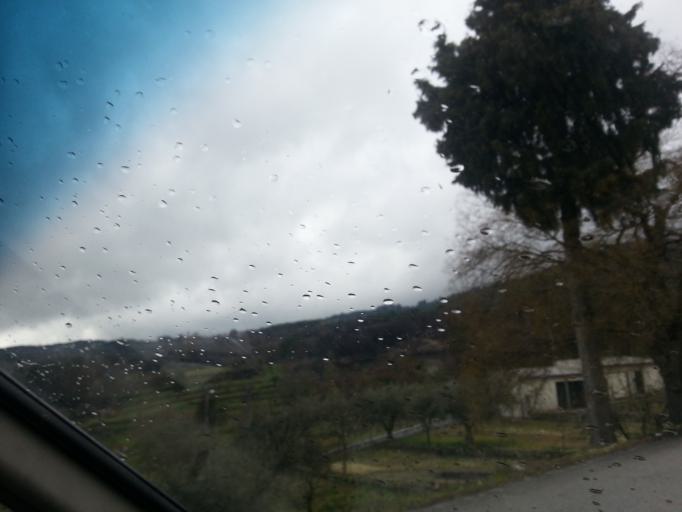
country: PT
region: Guarda
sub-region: Fornos de Algodres
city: Fornos de Algodres
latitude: 40.6197
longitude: -7.5866
